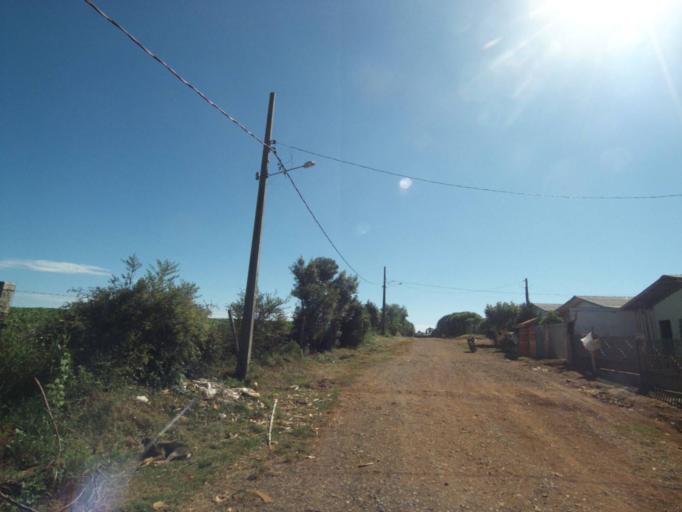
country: BR
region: Parana
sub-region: Pinhao
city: Pinhao
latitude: -25.8342
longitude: -52.0336
